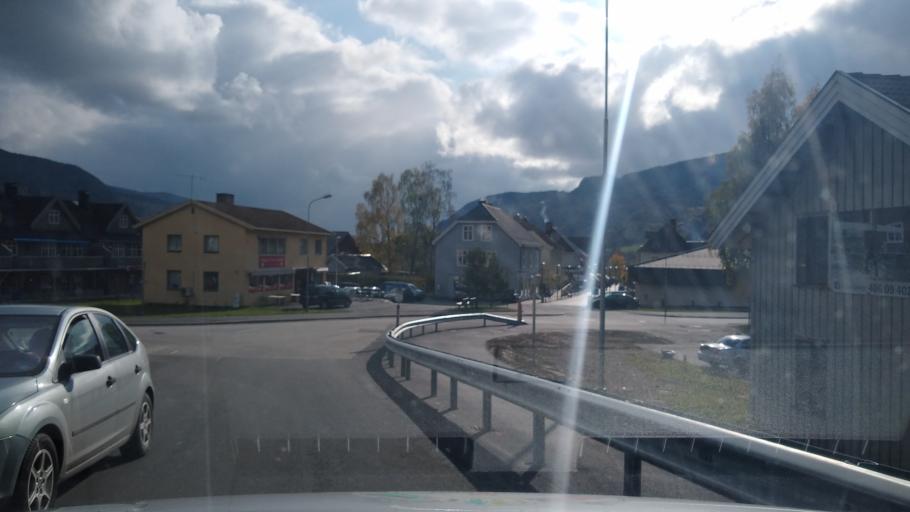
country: NO
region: Oppland
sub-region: Ringebu
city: Ringebu
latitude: 61.5321
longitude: 10.1390
